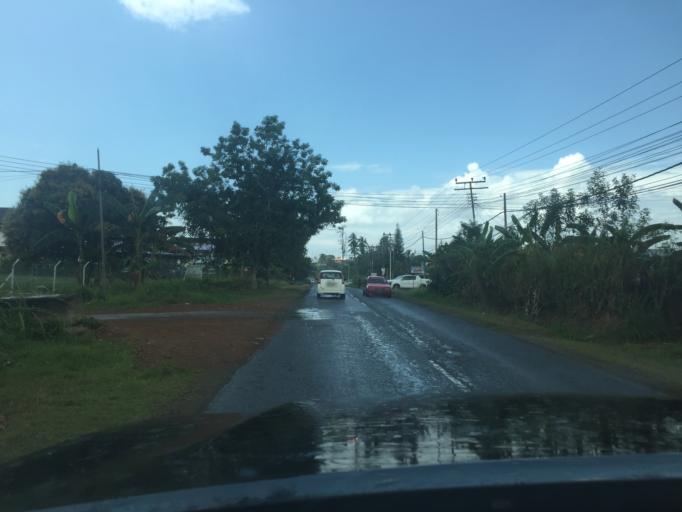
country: MY
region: Sabah
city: Lahad Datu
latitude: 5.0450
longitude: 118.3391
